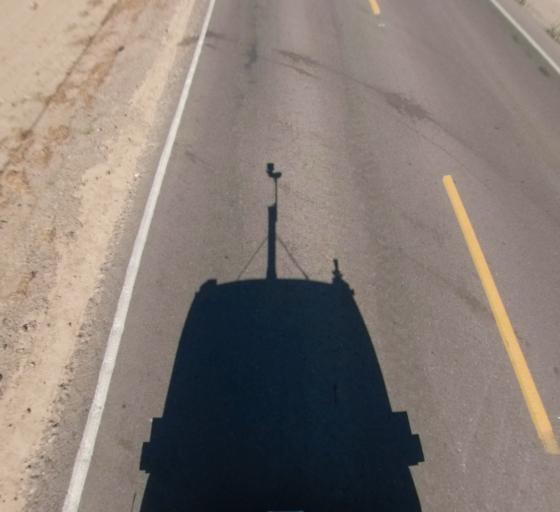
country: US
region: California
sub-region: Fresno County
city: Biola
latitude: 36.8513
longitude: -120.0168
